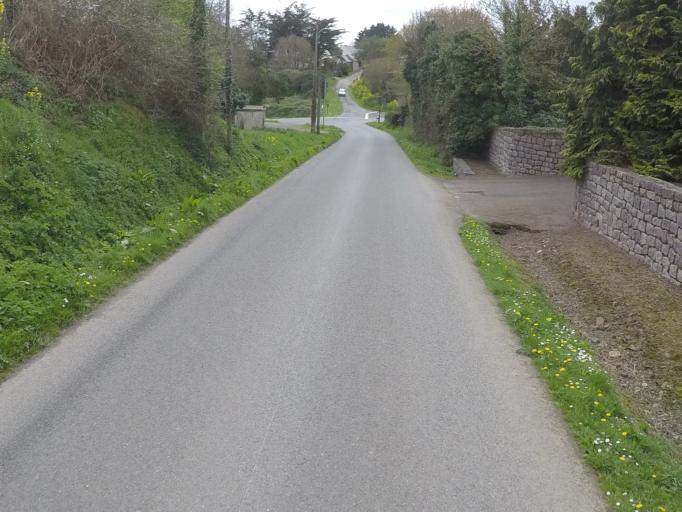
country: FR
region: Brittany
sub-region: Departement des Cotes-d'Armor
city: Plouezec
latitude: 48.7359
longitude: -2.9552
